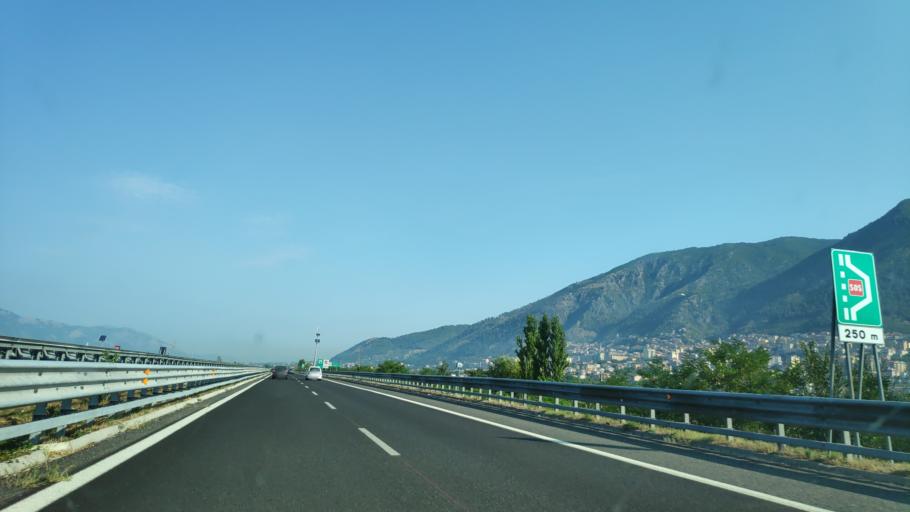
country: IT
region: Campania
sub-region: Provincia di Salerno
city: Sala Consilina
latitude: 40.3808
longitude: 15.5945
